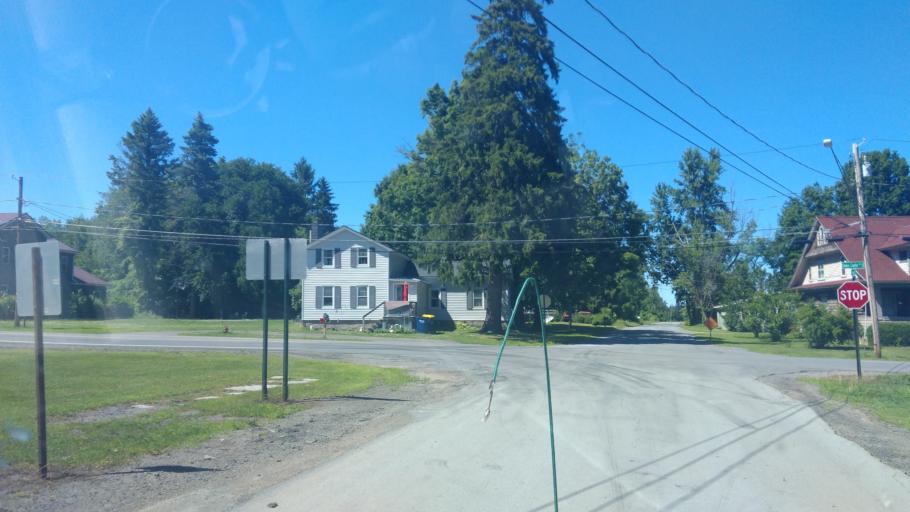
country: US
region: New York
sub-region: Wayne County
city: Sodus
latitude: 43.2042
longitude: -77.0248
